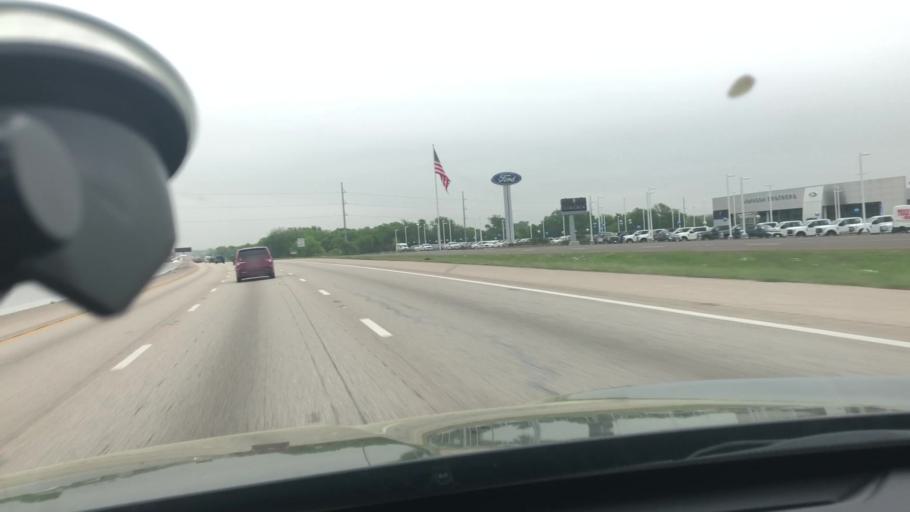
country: US
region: Texas
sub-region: Bell County
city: Belton
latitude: 31.0613
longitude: -97.4350
